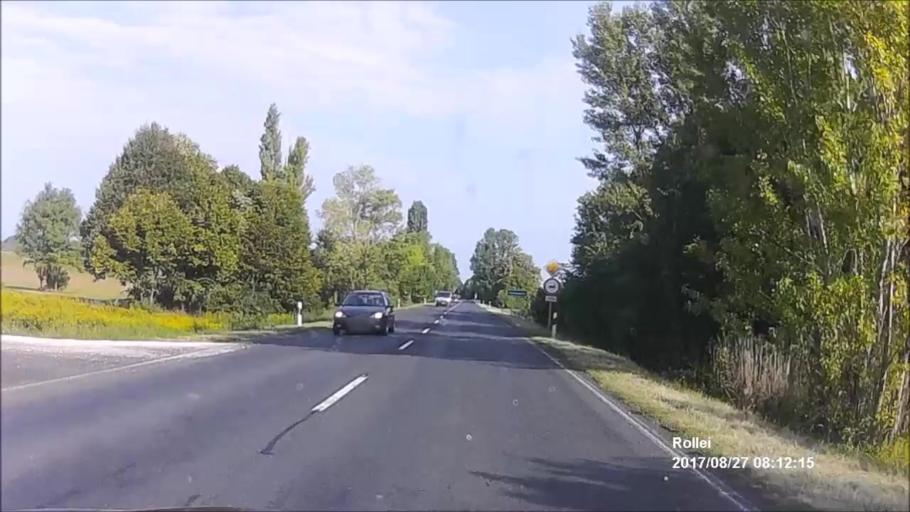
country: HU
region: Veszprem
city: Tapolca
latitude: 46.8294
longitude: 17.3778
